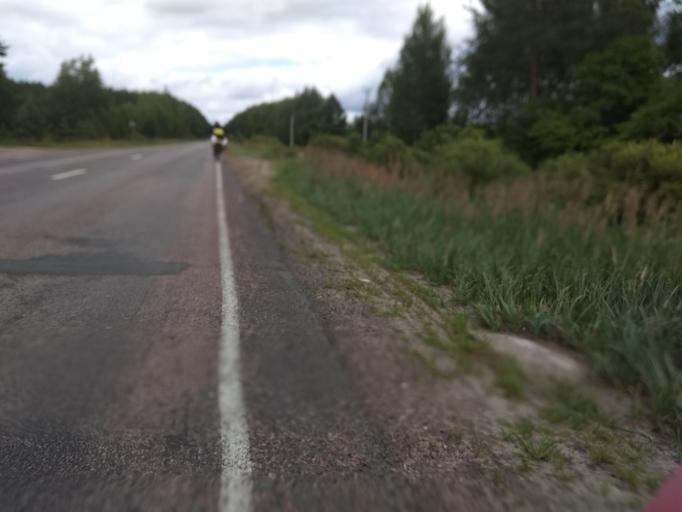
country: RU
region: Moskovskaya
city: Misheronskiy
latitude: 55.6082
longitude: 39.7132
